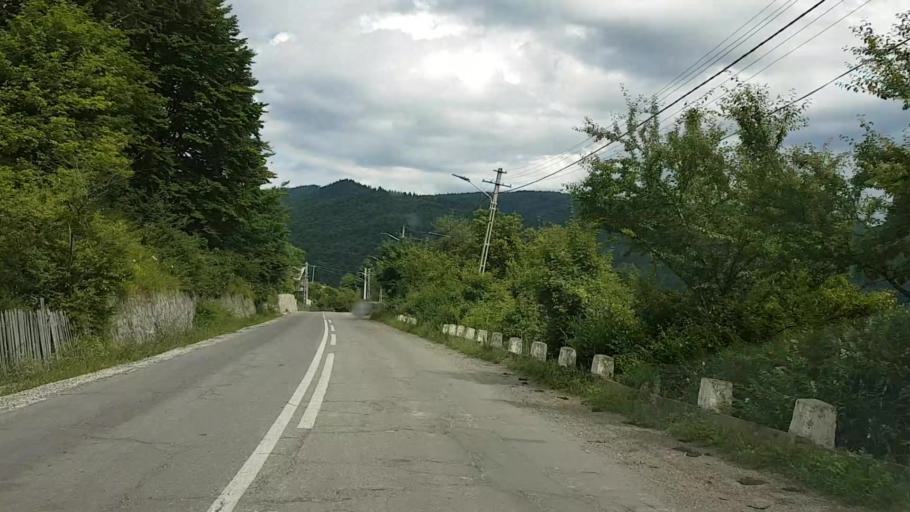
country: RO
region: Neamt
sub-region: Comuna Bicaz
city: Dodeni
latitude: 46.9867
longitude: 26.1026
